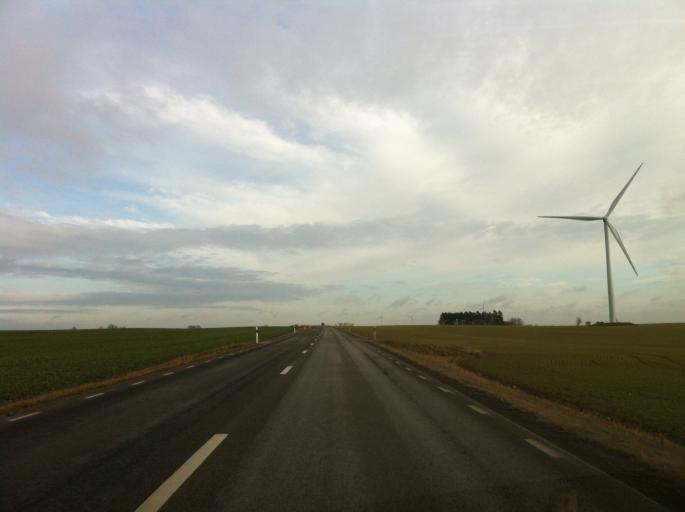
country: SE
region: Skane
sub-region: Svalovs Kommun
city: Teckomatorp
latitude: 55.8916
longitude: 13.0204
